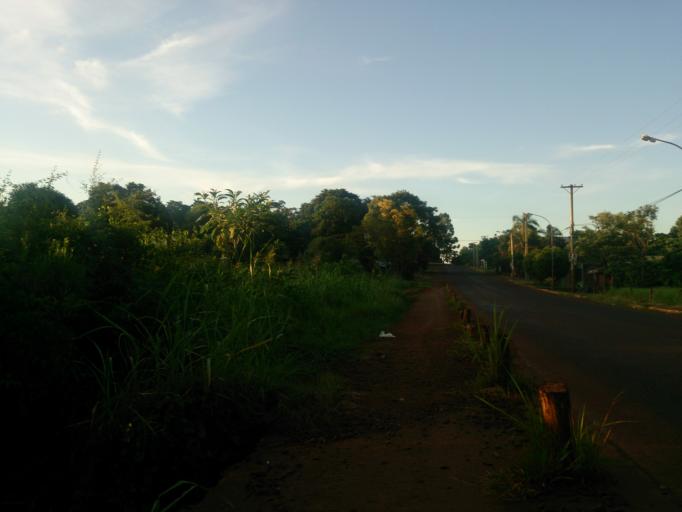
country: AR
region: Misiones
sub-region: Departamento de Obera
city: Obera
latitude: -27.4968
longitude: -55.1130
